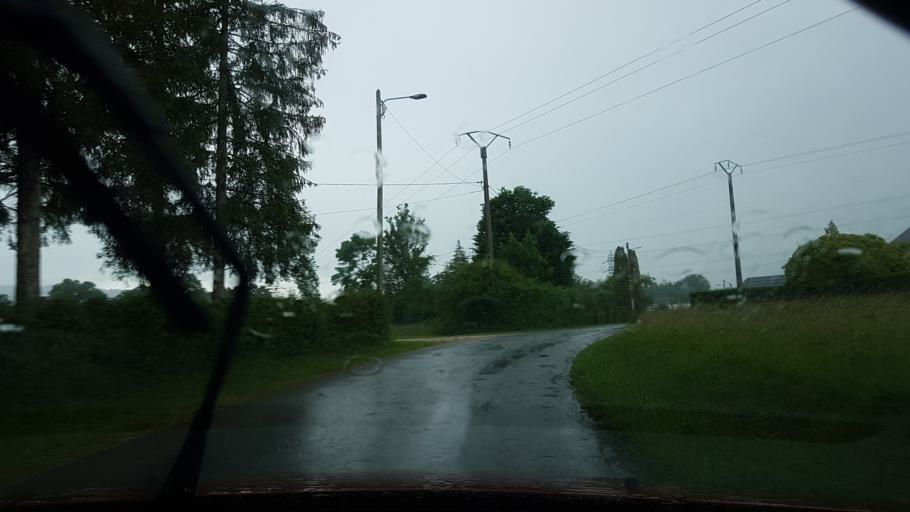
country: FR
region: Franche-Comte
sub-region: Departement du Jura
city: Clairvaux-les-Lacs
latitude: 46.5780
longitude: 5.6942
